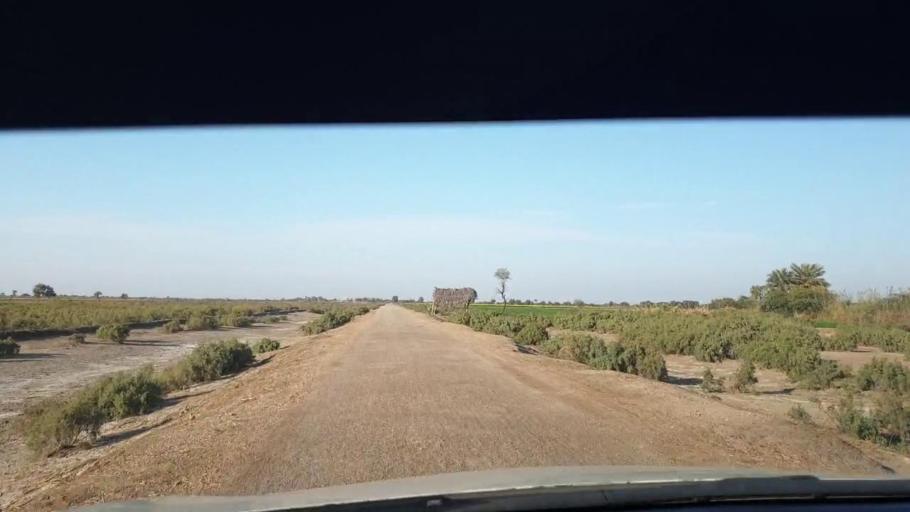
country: PK
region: Sindh
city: Berani
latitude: 25.8092
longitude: 68.9102
